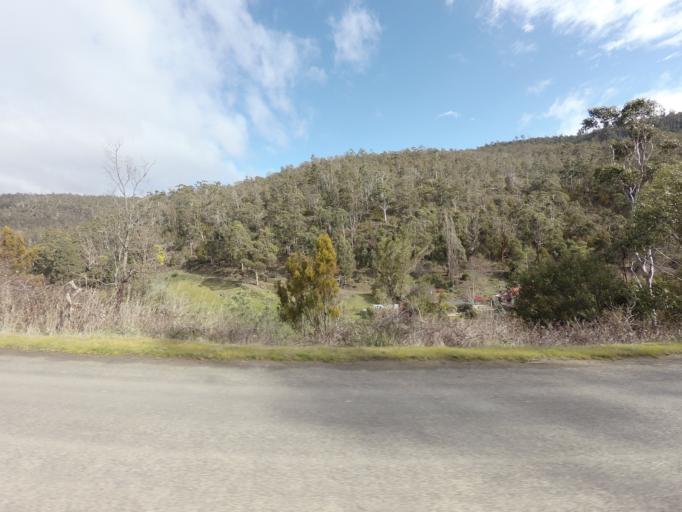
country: AU
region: Tasmania
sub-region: Derwent Valley
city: New Norfolk
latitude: -42.7869
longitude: 146.9467
